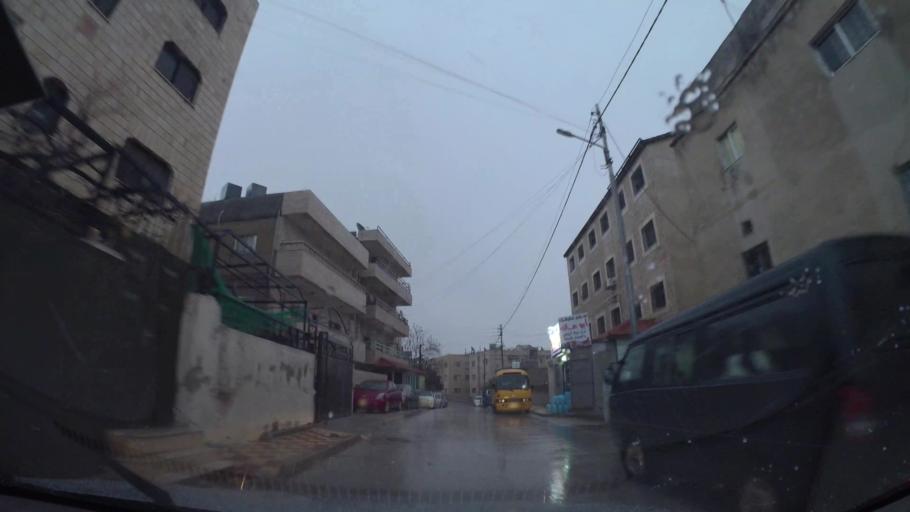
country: JO
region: Amman
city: Al Jubayhah
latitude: 32.0272
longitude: 35.8445
